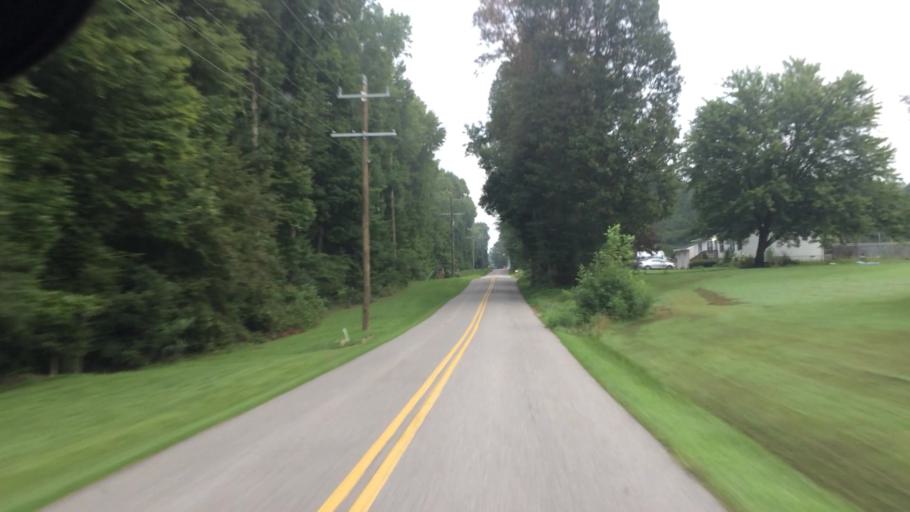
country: US
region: Virginia
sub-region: King William County
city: West Point
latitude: 37.5620
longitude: -76.7063
